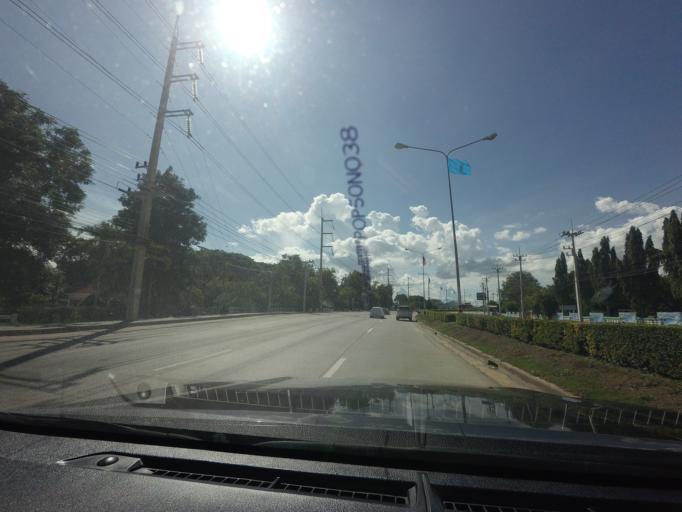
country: TH
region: Suphan Buri
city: Song Phi Nong
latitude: 14.1818
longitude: 99.9364
